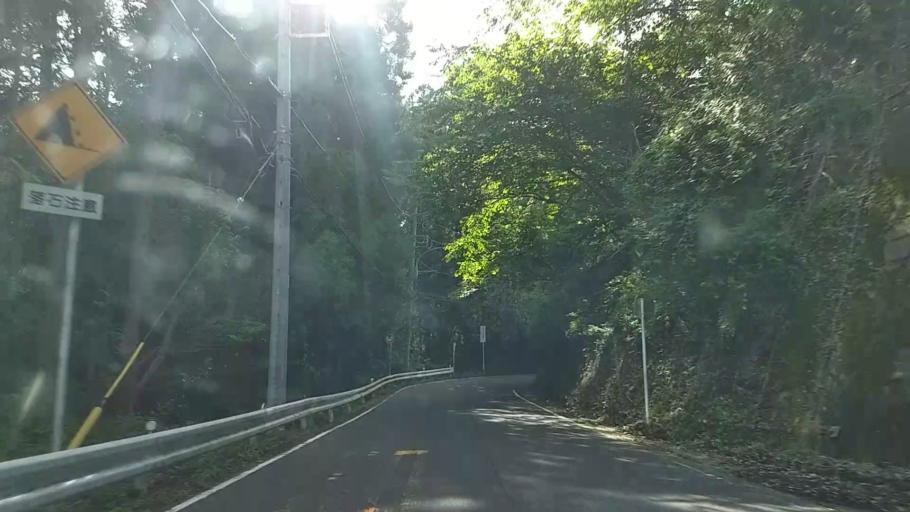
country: JP
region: Yamanashi
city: Uenohara
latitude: 35.5662
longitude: 139.1469
